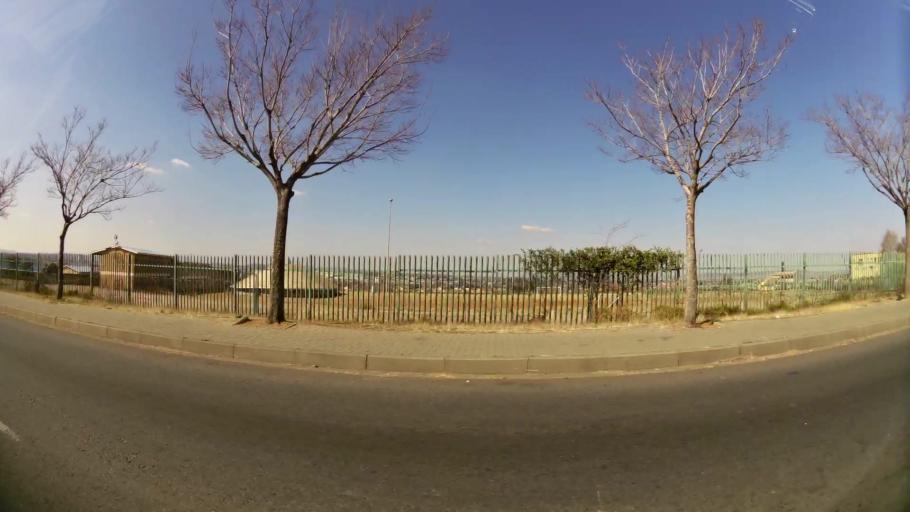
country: ZA
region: Gauteng
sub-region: City of Johannesburg Metropolitan Municipality
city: Soweto
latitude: -26.2728
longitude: 27.8732
